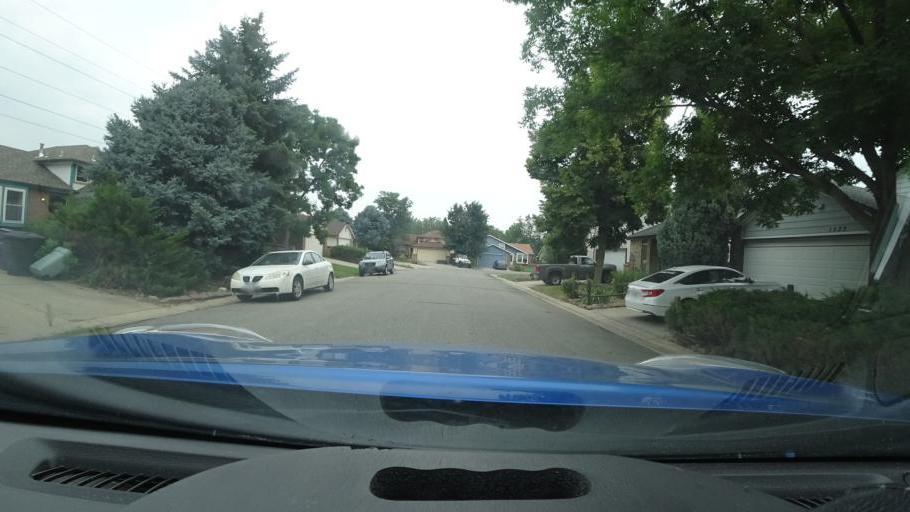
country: US
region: Colorado
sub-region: Arapahoe County
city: Glendale
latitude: 39.6885
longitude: -104.9172
